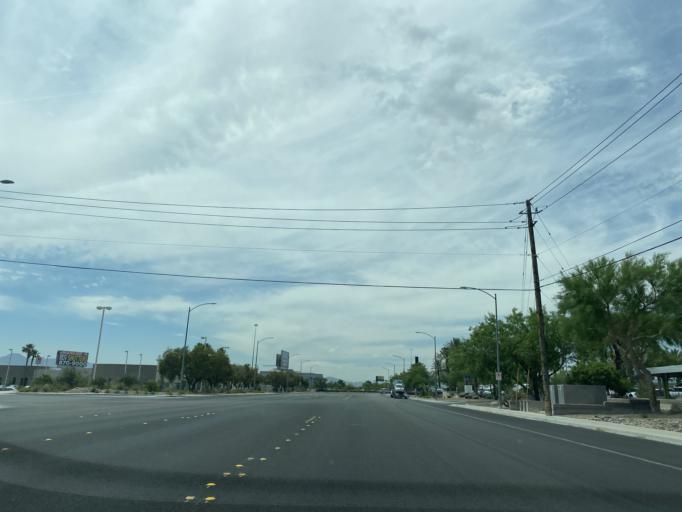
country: US
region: Nevada
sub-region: Clark County
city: Paradise
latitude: 36.0664
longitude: -115.1545
